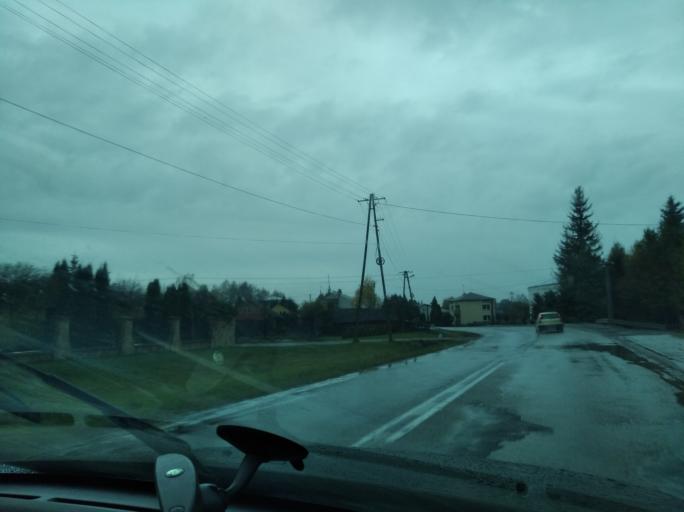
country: PL
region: Subcarpathian Voivodeship
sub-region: Powiat lancucki
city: Albigowa
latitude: 50.0146
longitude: 22.2243
